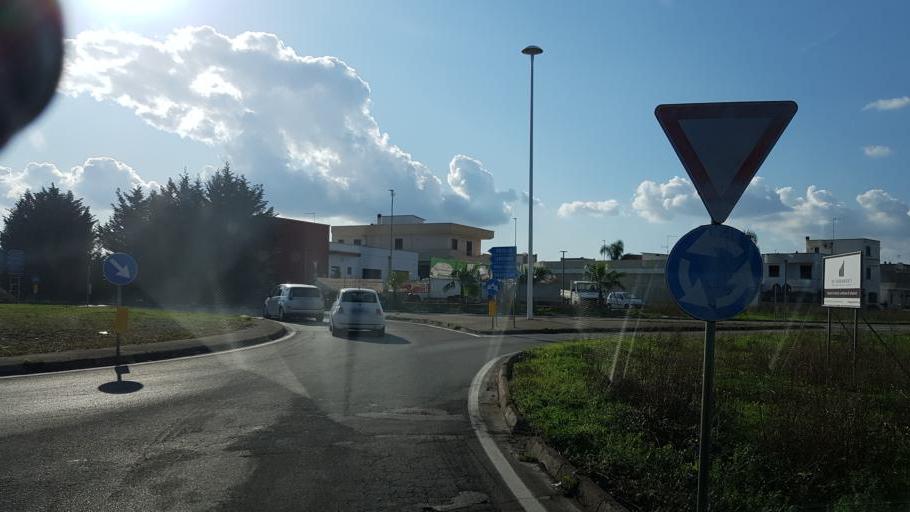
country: IT
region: Apulia
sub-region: Provincia di Lecce
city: Salice Salentino
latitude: 40.3809
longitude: 17.9698
